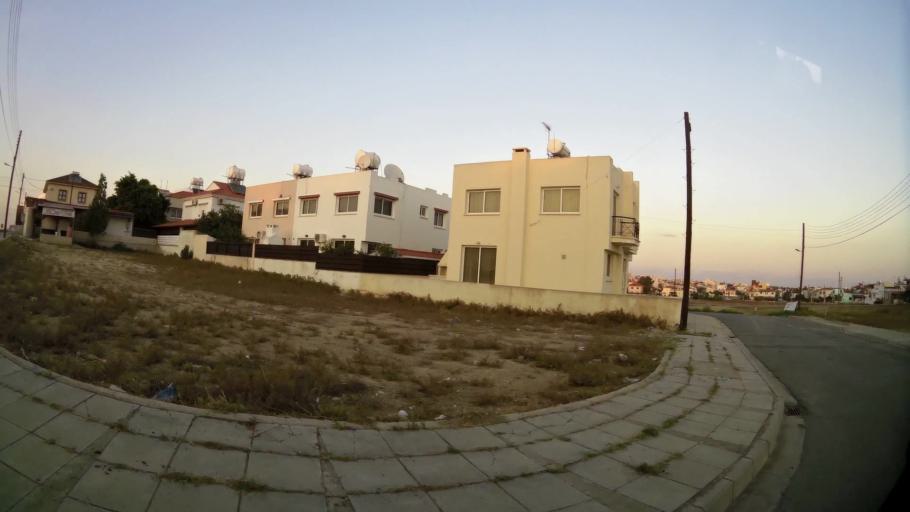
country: CY
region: Larnaka
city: Larnaca
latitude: 34.9136
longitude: 33.5893
